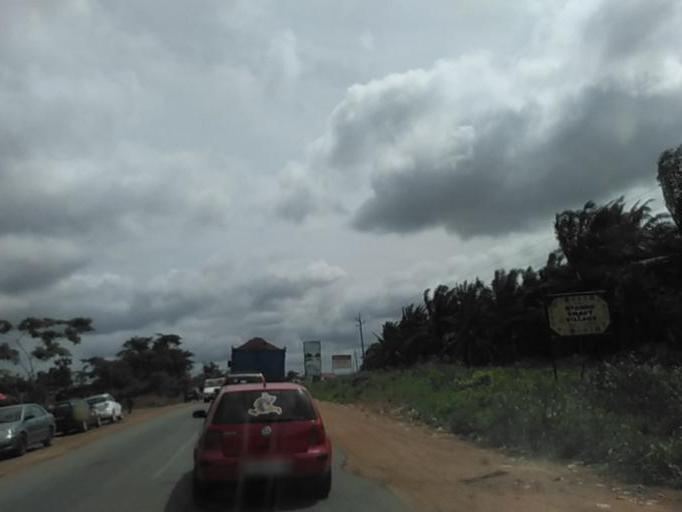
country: GH
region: Ashanti
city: Mamponteng
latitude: 6.7675
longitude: -1.4558
